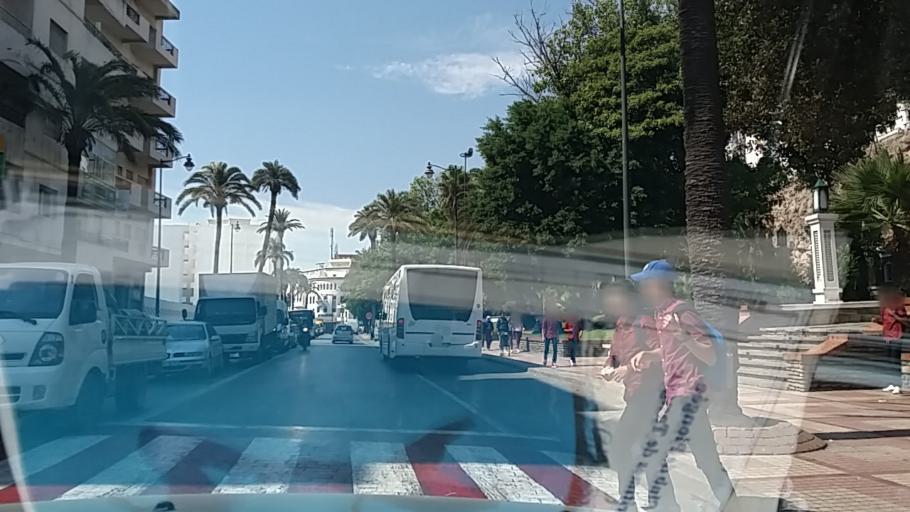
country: MA
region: Tanger-Tetouan
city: Tetouan
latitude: 35.5680
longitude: -5.3737
